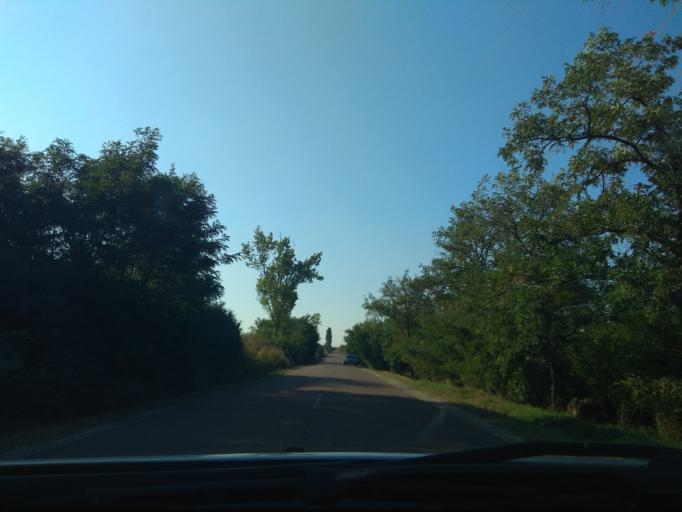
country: HU
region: Borsod-Abauj-Zemplen
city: Nyekladhaza
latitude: 47.9716
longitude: 20.7967
